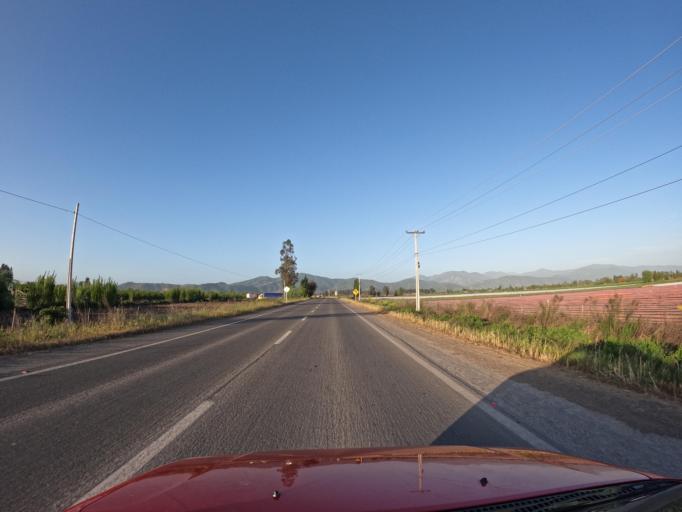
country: CL
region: O'Higgins
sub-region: Provincia de Cachapoal
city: San Vicente
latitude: -34.3007
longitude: -71.3755
